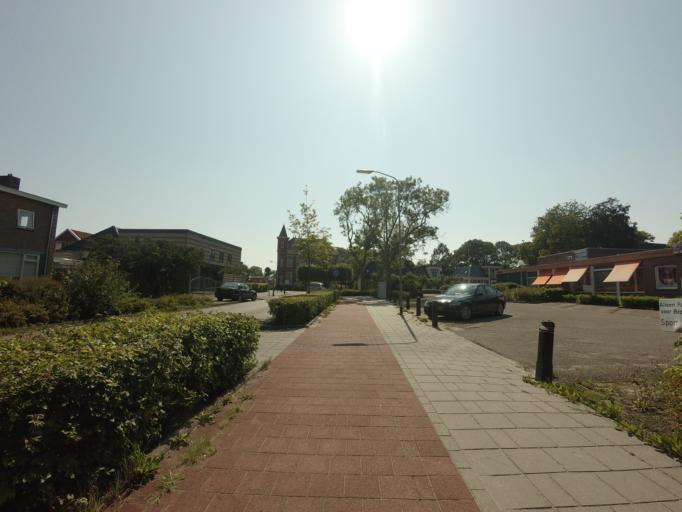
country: NL
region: Groningen
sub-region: Gemeente Zuidhorn
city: Grijpskerk
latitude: 53.2643
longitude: 6.3062
